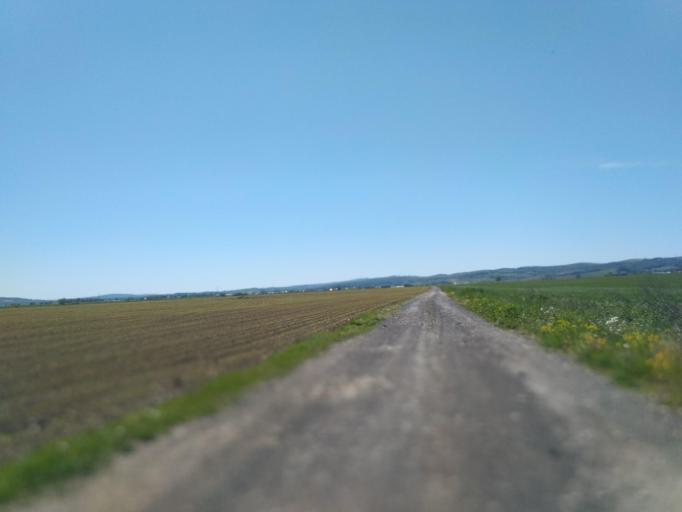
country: PL
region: Subcarpathian Voivodeship
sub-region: Powiat sanocki
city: Besko
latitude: 49.6121
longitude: 21.9742
